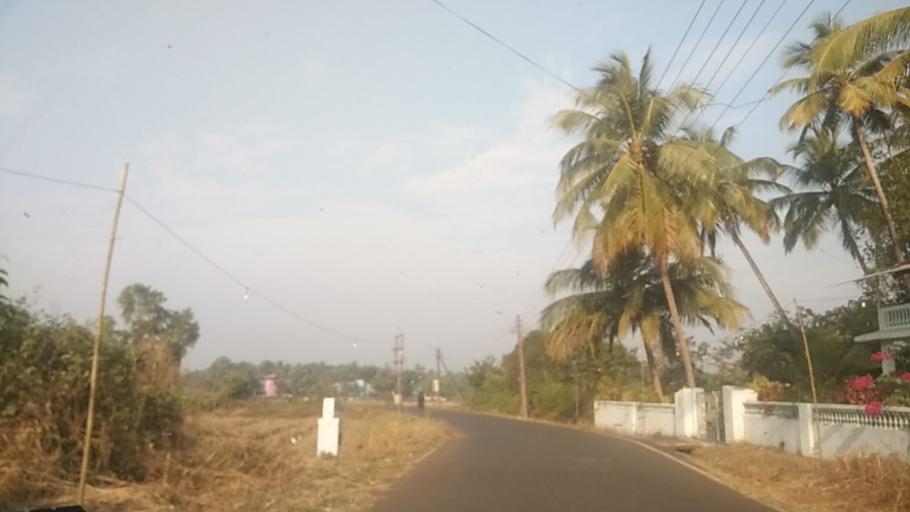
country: IN
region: Goa
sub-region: South Goa
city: Chinchinim
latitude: 15.2373
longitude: 73.9811
